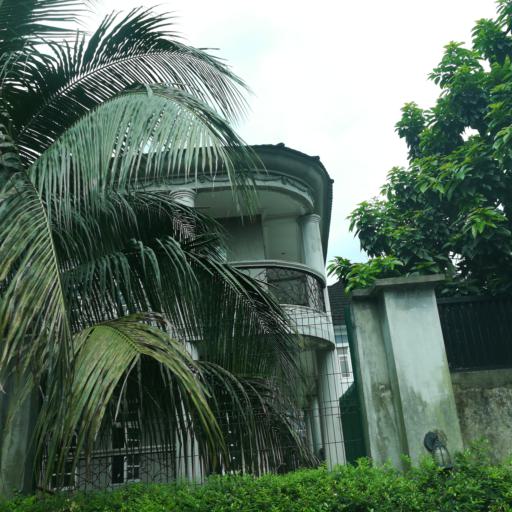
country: NG
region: Rivers
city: Port Harcourt
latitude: 4.8250
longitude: 6.9858
